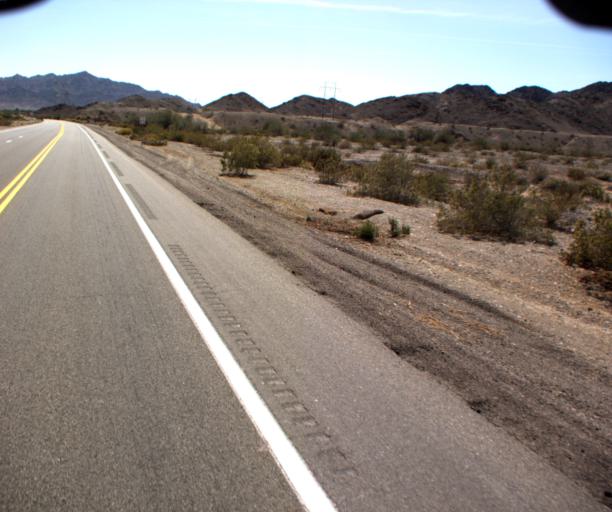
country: US
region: Arizona
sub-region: Yuma County
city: Fortuna Foothills
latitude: 32.7955
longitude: -114.3813
